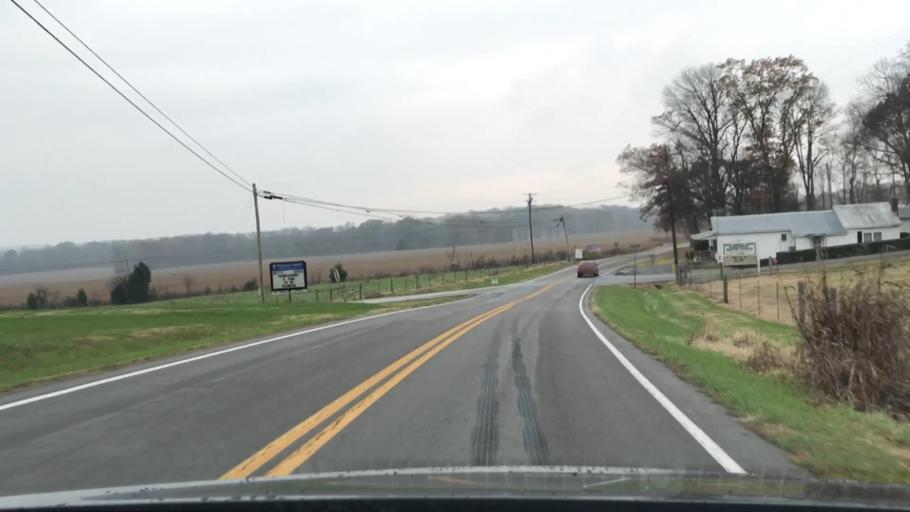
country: US
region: Tennessee
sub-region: Sumner County
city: Portland
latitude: 36.6960
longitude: -86.3939
